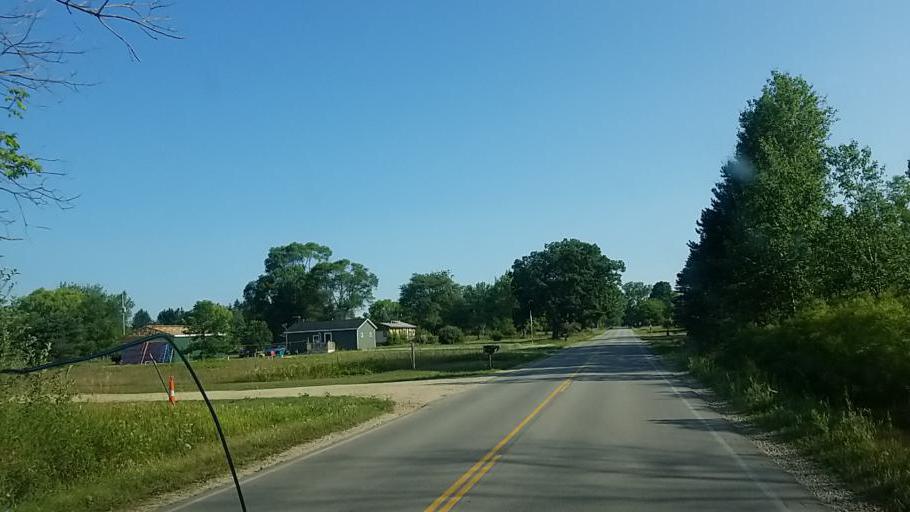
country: US
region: Michigan
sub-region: Newaygo County
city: Fremont
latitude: 43.3755
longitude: -85.9394
